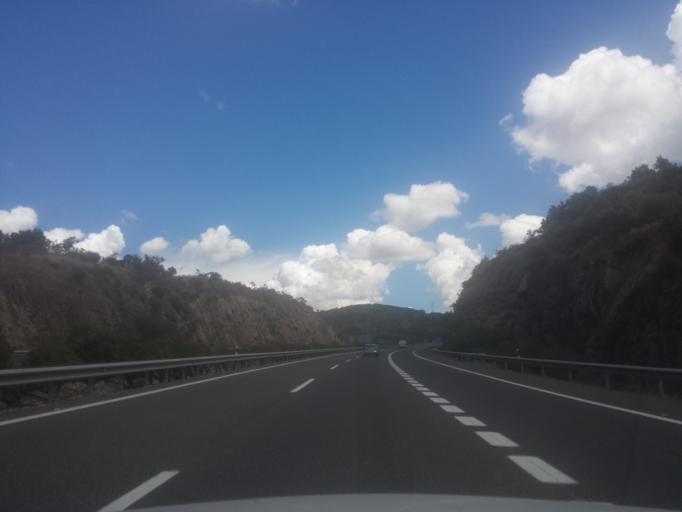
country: ES
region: Extremadura
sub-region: Provincia de Caceres
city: Aldeanueva del Camino
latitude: 40.2718
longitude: -5.9123
